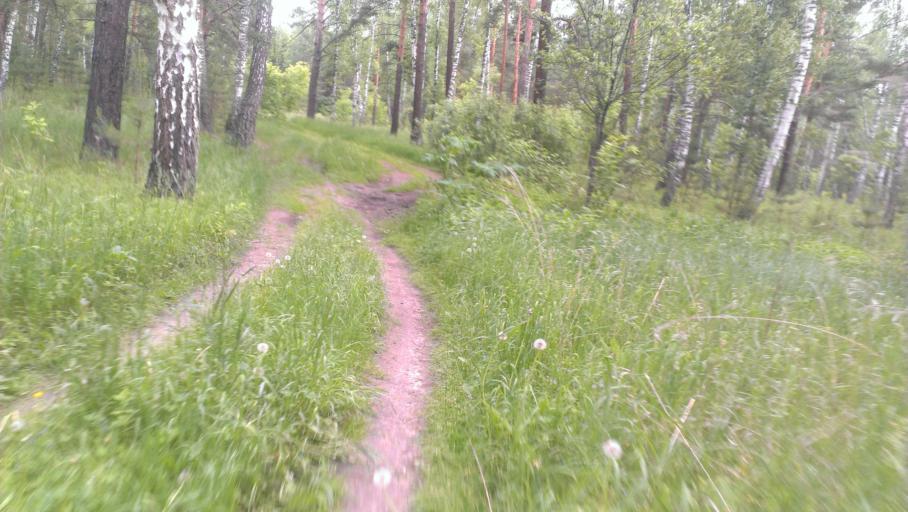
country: RU
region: Altai Krai
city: Sannikovo
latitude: 53.3449
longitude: 84.0427
